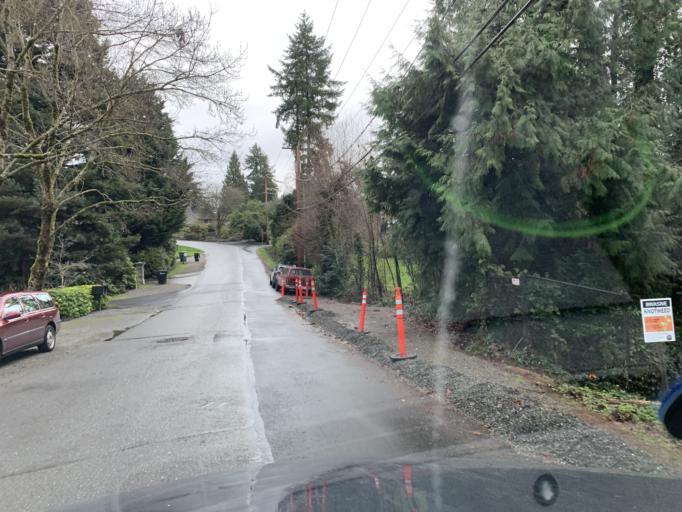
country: US
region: Washington
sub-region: King County
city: Mercer Island
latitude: 47.5913
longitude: -122.2361
